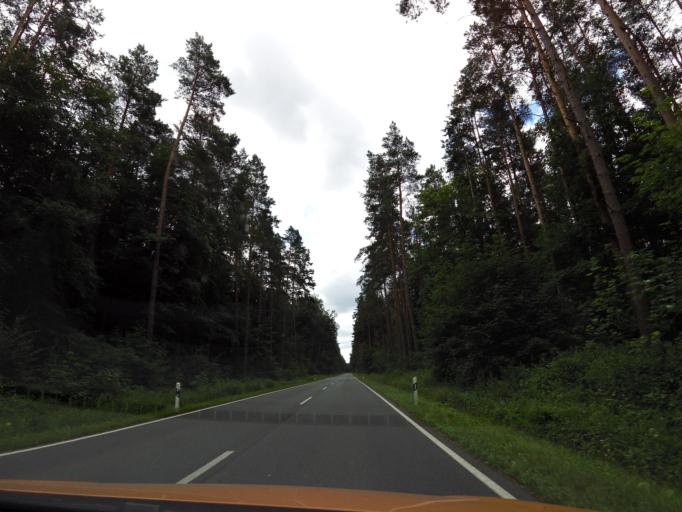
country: DE
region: Mecklenburg-Vorpommern
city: Krakow am See
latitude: 53.6083
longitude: 12.2547
